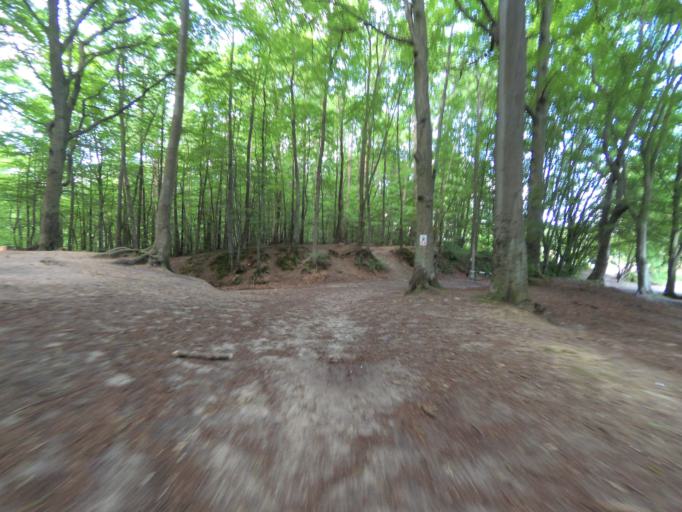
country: PL
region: Pomeranian Voivodeship
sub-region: Gdynia
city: Wielki Kack
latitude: 54.4921
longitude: 18.5059
